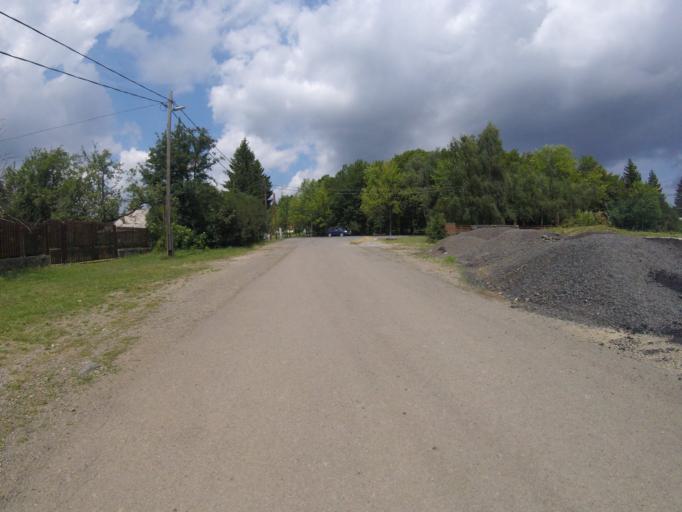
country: HU
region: Nograd
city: Batonyterenye
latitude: 47.9057
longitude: 19.8785
